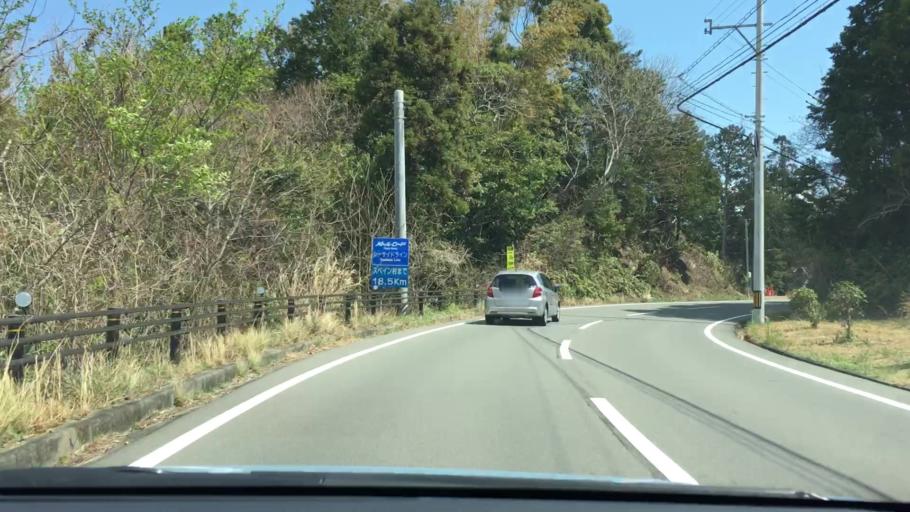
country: JP
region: Mie
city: Toba
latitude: 34.4420
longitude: 136.8872
